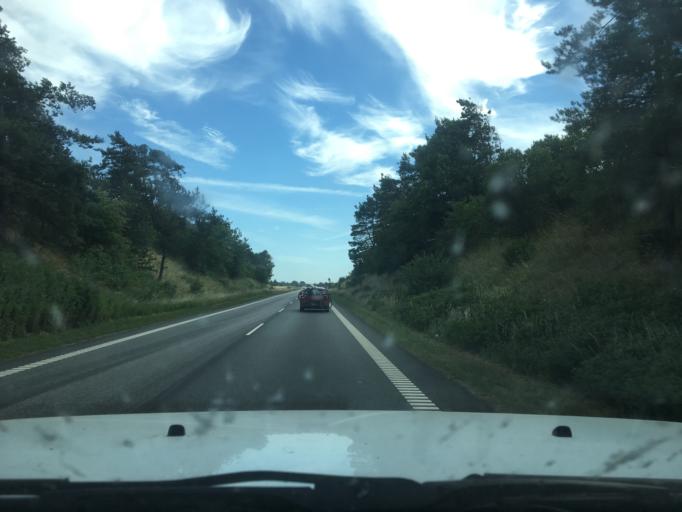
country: DK
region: Central Jutland
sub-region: Viborg Kommune
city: Viborg
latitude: 56.5620
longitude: 9.3858
